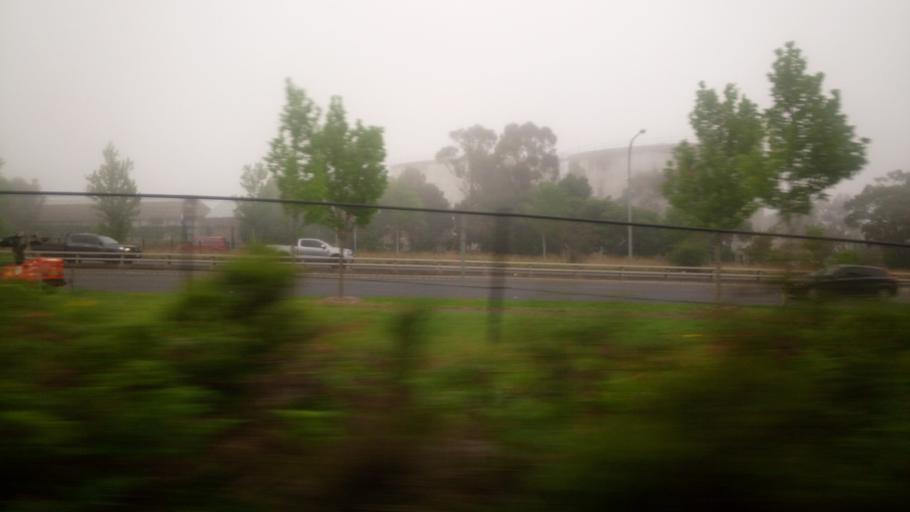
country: AU
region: New South Wales
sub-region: Blue Mountains Municipality
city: Leura
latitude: -33.7124
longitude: 150.3374
